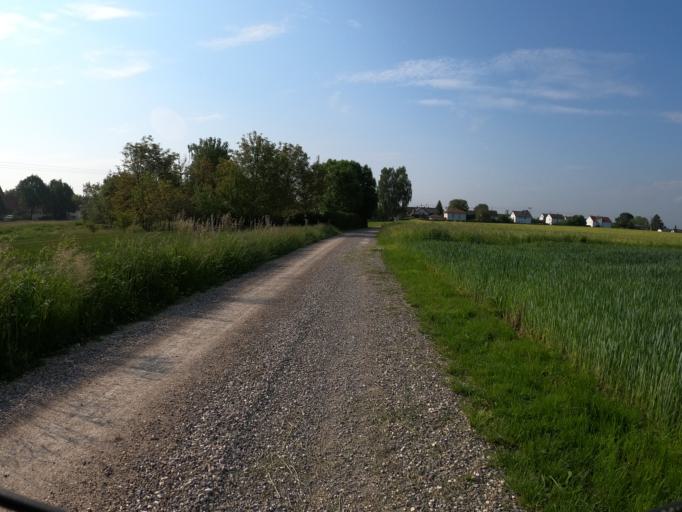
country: DE
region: Bavaria
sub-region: Swabia
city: Pfaffenhofen an der Roth
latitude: 48.3712
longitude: 10.1498
